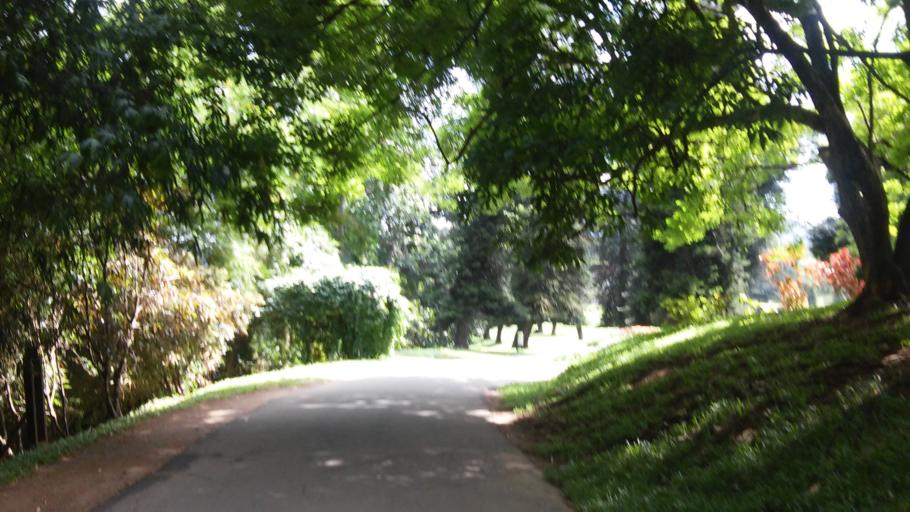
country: LK
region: Central
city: Kandy
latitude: 7.2686
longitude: 80.5940
